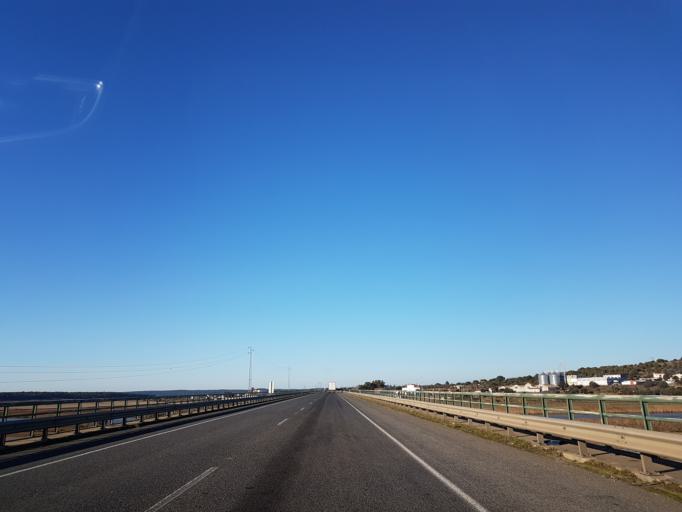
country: PT
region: Setubal
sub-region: Alcacer do Sal
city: Alcacer do Sal
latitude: 38.3658
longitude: -8.5236
